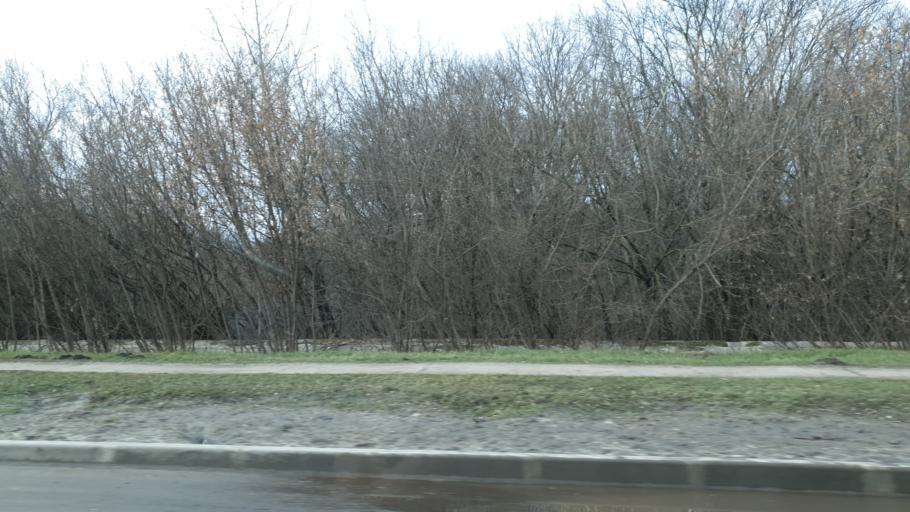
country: RU
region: Kursk
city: Kursk
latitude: 51.6830
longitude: 36.1499
